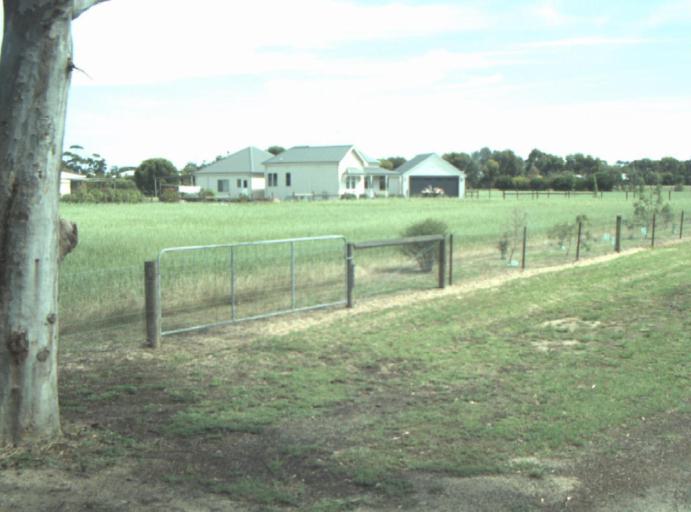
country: AU
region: Victoria
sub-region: Wyndham
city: Little River
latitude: -37.9688
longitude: 144.5067
